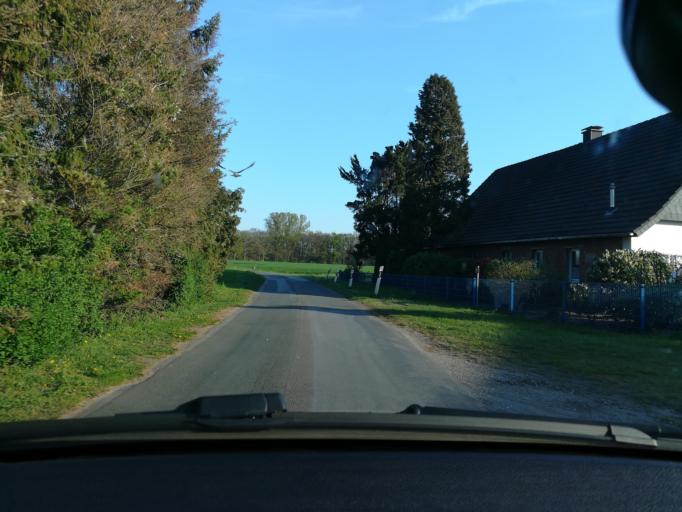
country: DE
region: North Rhine-Westphalia
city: Versmold
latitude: 52.0194
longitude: 8.1013
